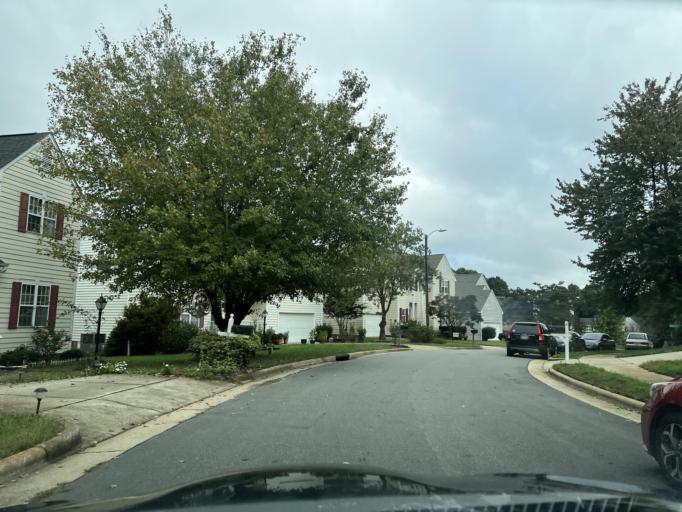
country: US
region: North Carolina
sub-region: Wake County
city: West Raleigh
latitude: 35.7483
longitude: -78.6846
